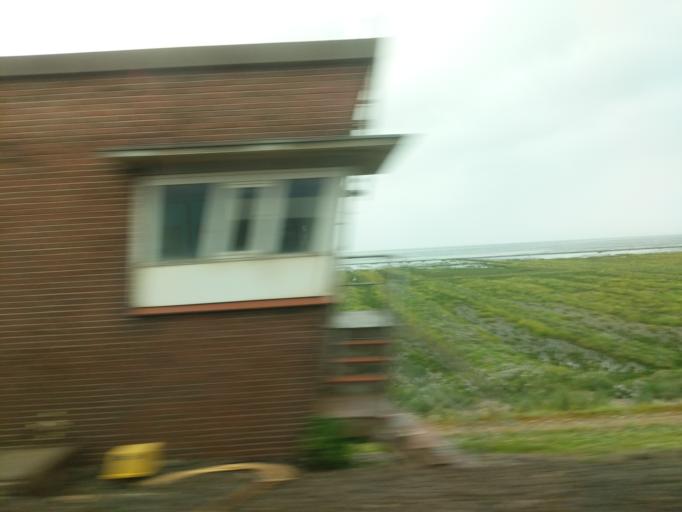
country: DE
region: Schleswig-Holstein
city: Friedrich-Wilhelm-Lubke-Koog
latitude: 54.8848
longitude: 8.5549
